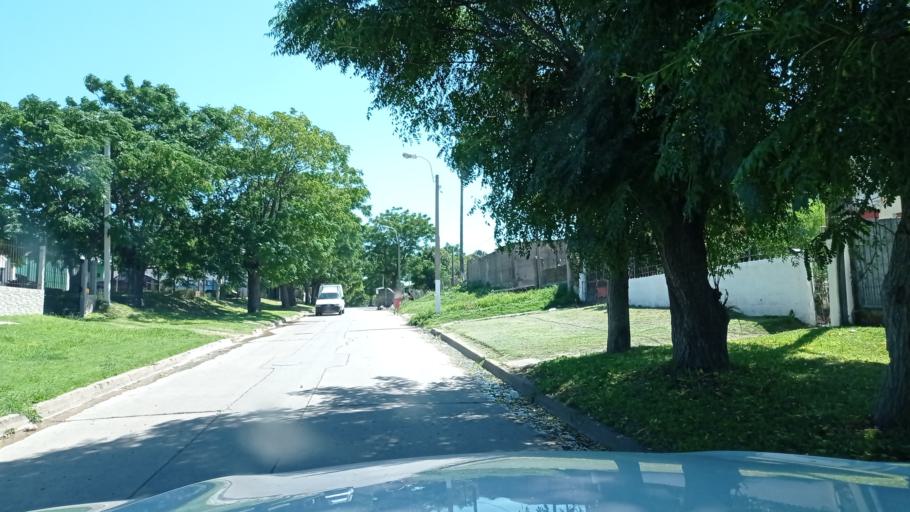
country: UY
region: Montevideo
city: Montevideo
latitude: -34.8658
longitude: -56.2629
